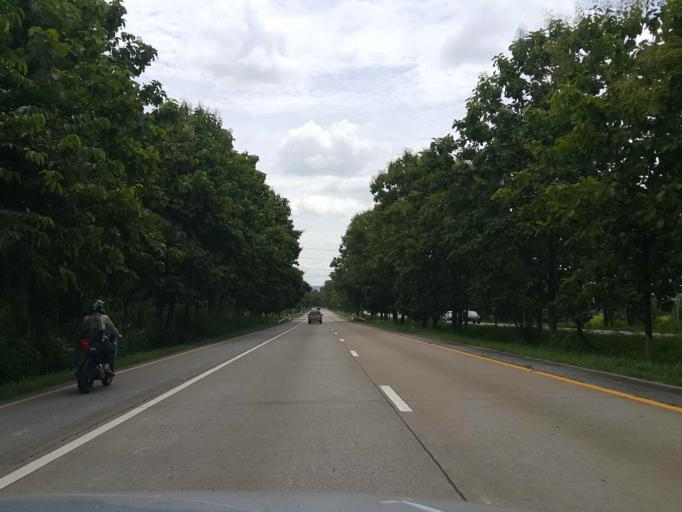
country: TH
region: Lamphun
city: Mae Tha
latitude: 18.4850
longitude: 99.1299
